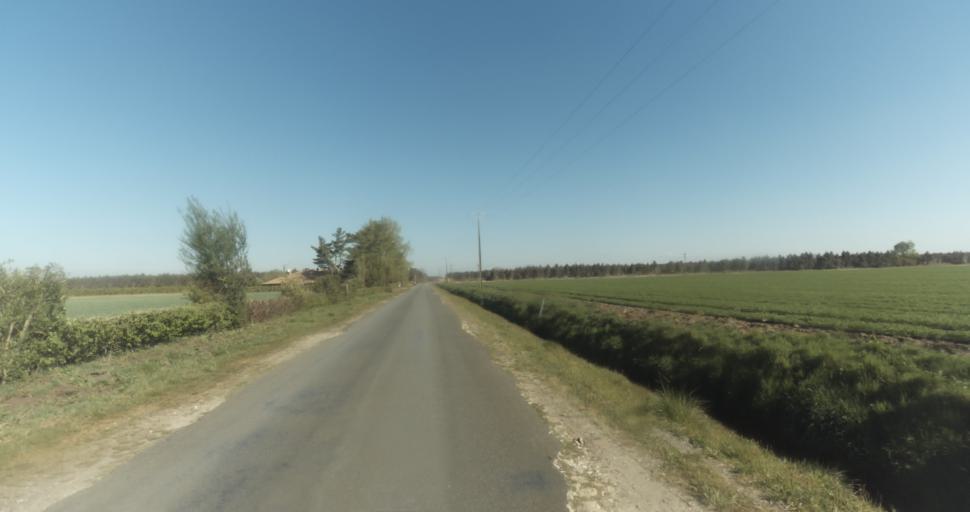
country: FR
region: Aquitaine
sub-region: Departement de la Gironde
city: Marcheprime
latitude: 44.7730
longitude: -0.8577
